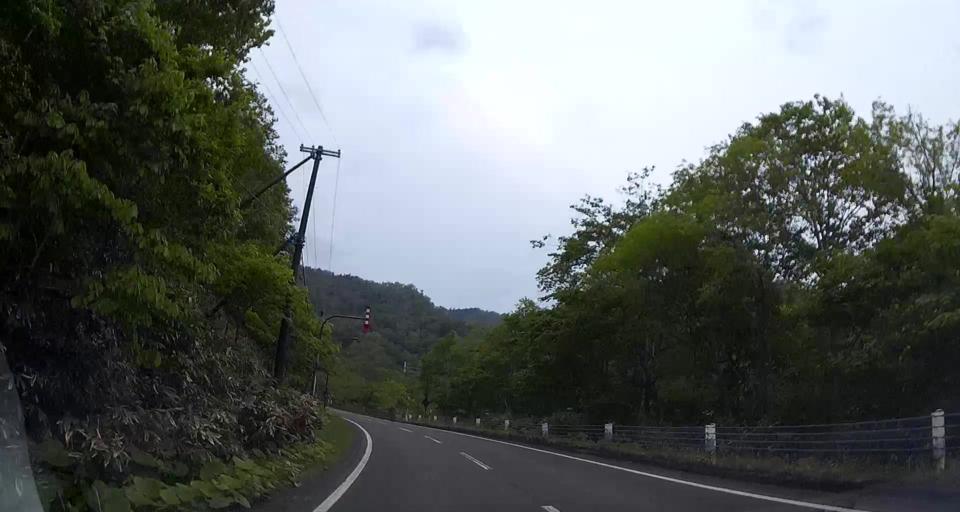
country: JP
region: Hokkaido
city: Shiraoi
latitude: 42.6549
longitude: 141.1861
